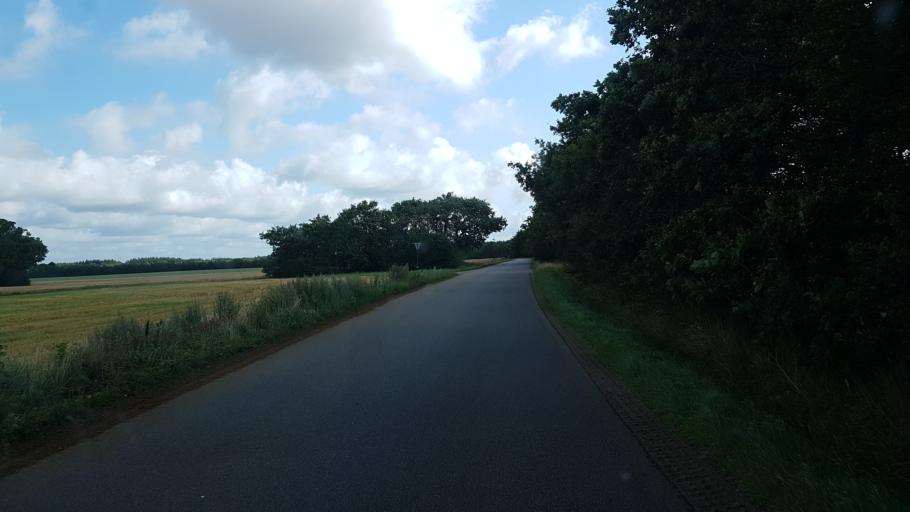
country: DK
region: South Denmark
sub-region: Varde Kommune
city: Olgod
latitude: 55.7839
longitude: 8.7251
